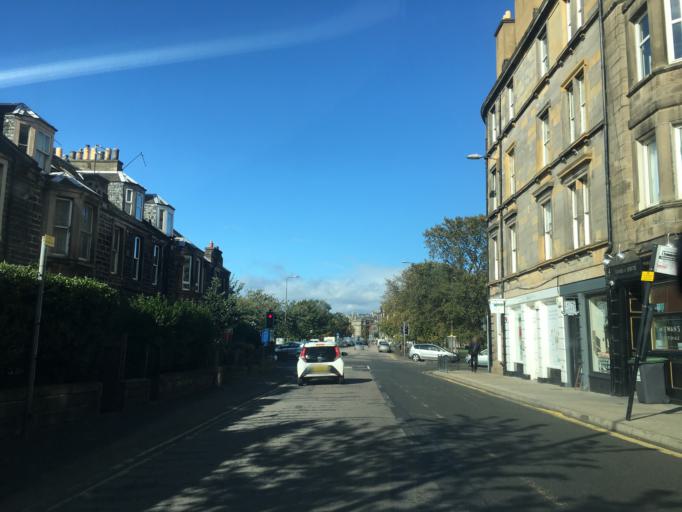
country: GB
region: Scotland
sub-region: West Lothian
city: Seafield
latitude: 55.9694
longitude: -3.1596
